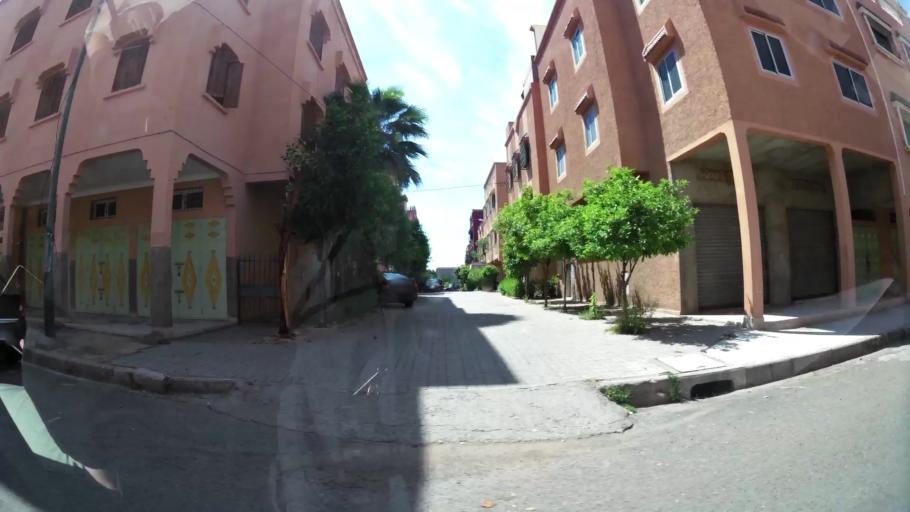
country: MA
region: Marrakech-Tensift-Al Haouz
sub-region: Marrakech
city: Marrakesh
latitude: 31.6412
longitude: -8.0632
